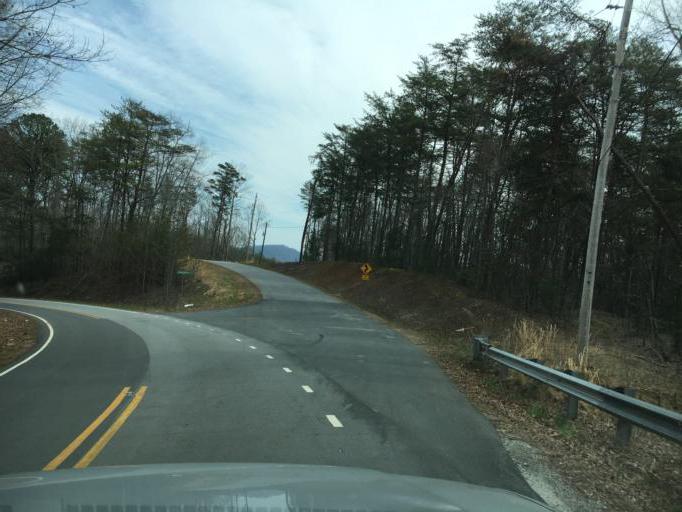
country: US
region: North Carolina
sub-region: Rutherford County
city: Lake Lure
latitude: 35.4829
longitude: -82.1179
